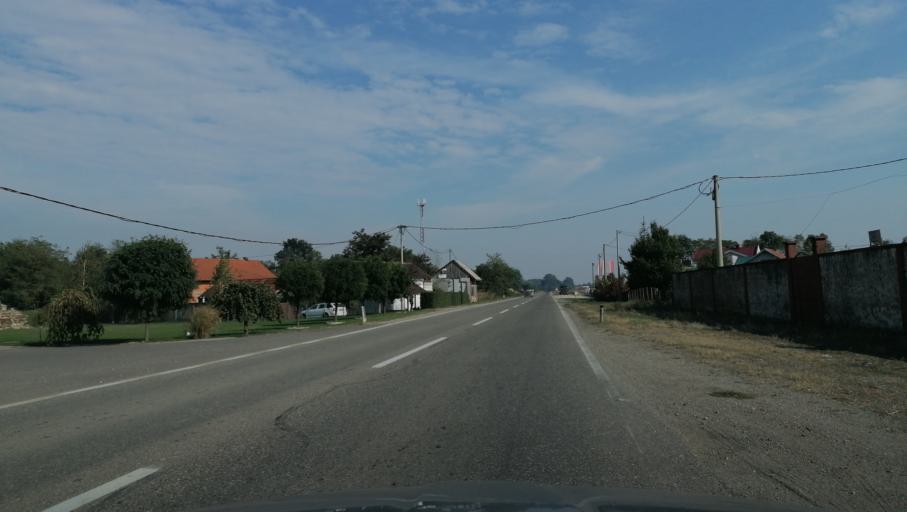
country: BA
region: Republika Srpska
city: Popovi
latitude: 44.7812
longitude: 19.2952
